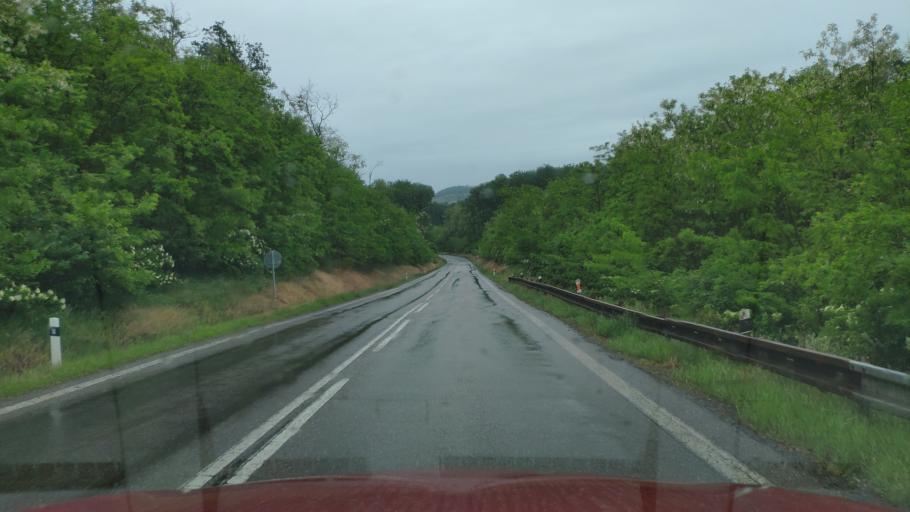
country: HU
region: Borsod-Abauj-Zemplen
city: Ricse
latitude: 48.4404
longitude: 21.9447
